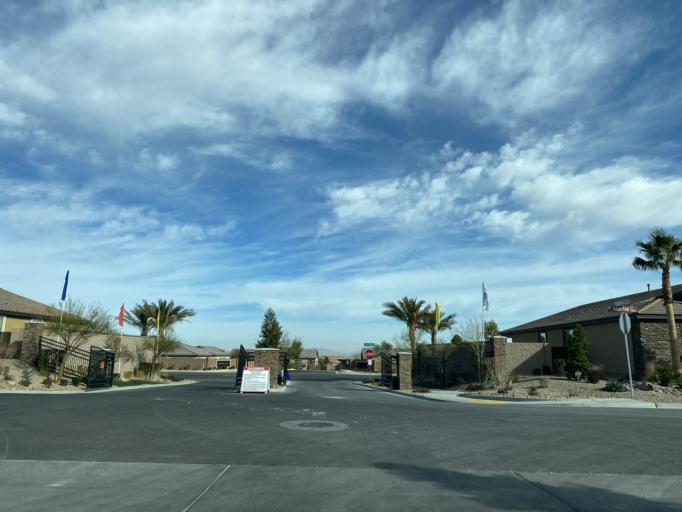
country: US
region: Nevada
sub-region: Clark County
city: Summerlin South
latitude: 36.2670
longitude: -115.3248
